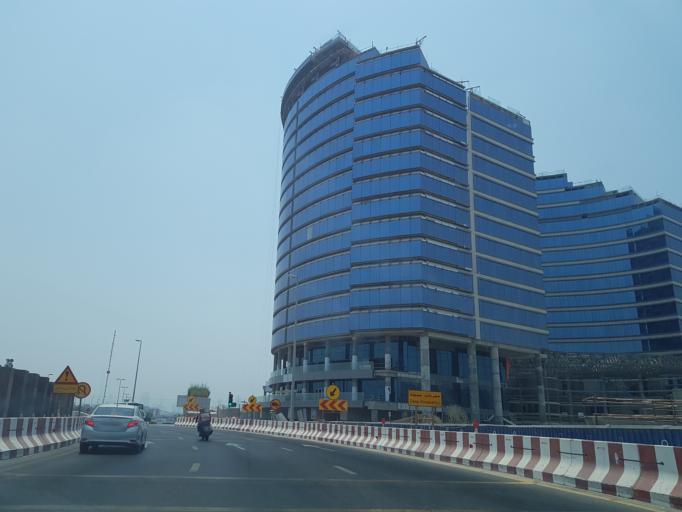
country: AE
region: Ash Shariqah
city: Sharjah
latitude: 25.2511
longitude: 55.3278
